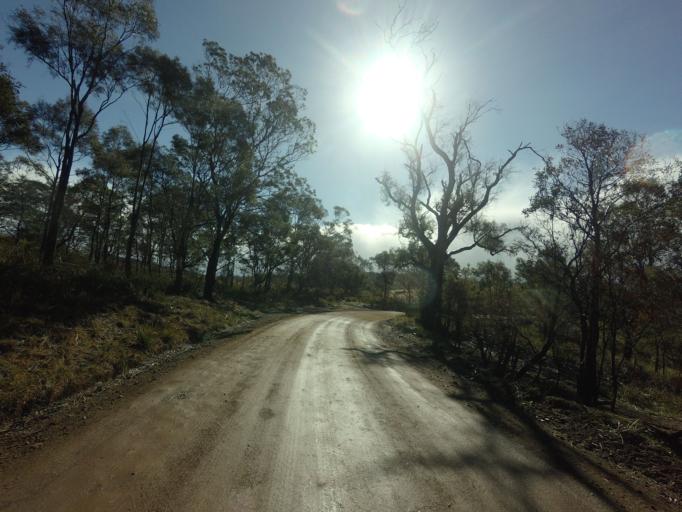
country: AU
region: Tasmania
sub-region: Sorell
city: Sorell
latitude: -42.4096
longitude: 147.9536
